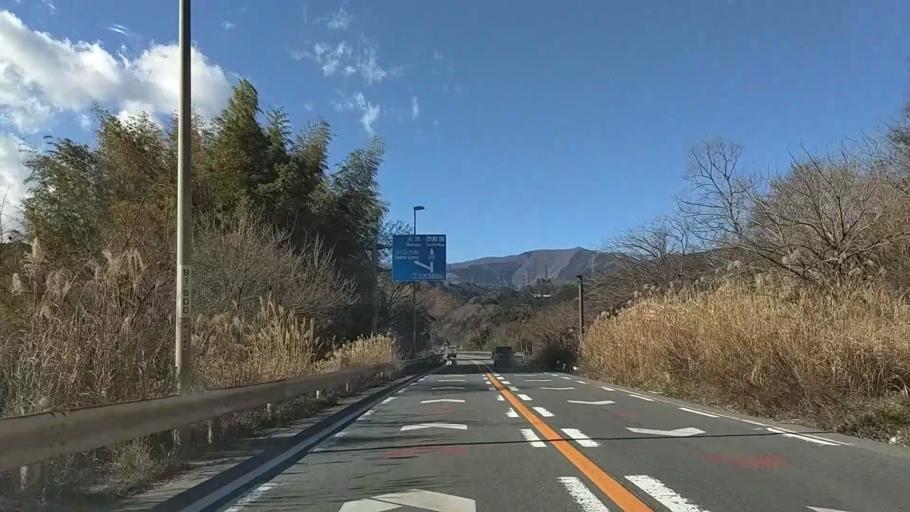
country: JP
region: Shizuoka
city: Gotemba
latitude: 35.3660
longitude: 138.9878
